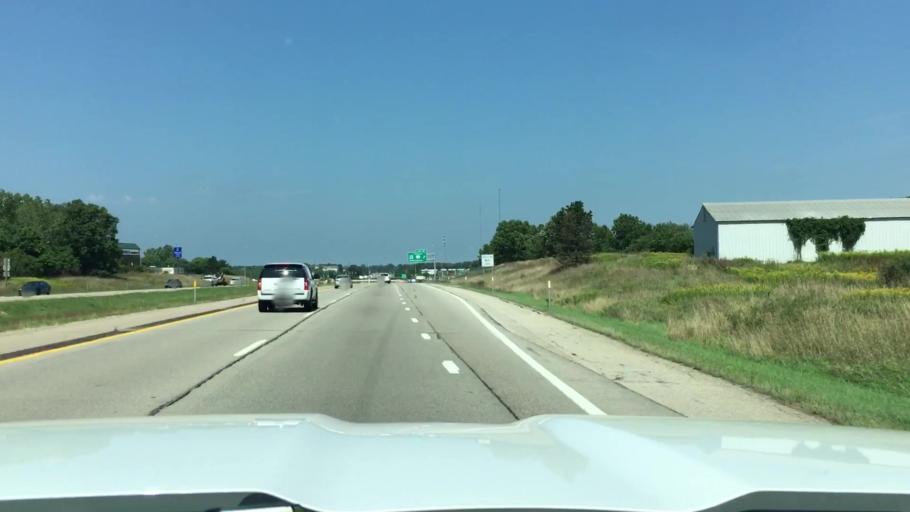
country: US
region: Michigan
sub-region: Kalamazoo County
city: Westwood
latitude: 42.2615
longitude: -85.6517
